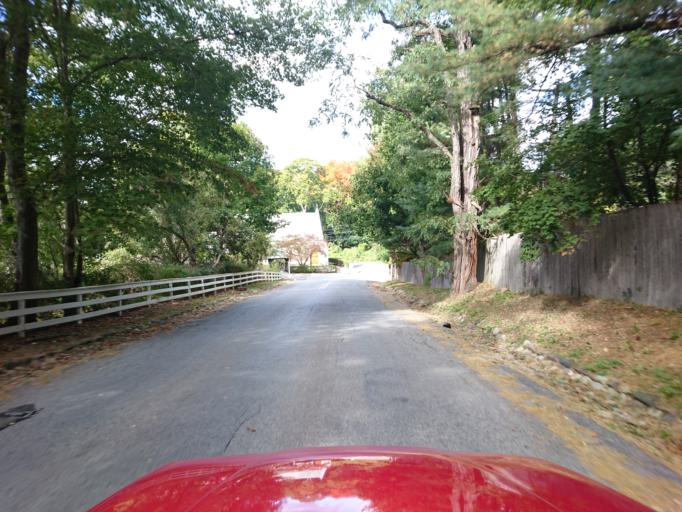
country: US
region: New York
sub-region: Nassau County
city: Lattingtown
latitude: 40.8880
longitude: -73.6080
